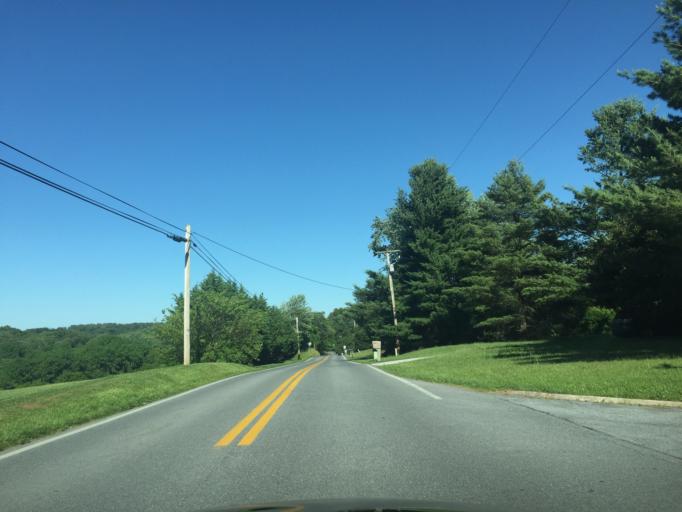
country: US
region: Maryland
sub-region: Carroll County
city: Hampstead
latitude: 39.5607
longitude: -76.9089
